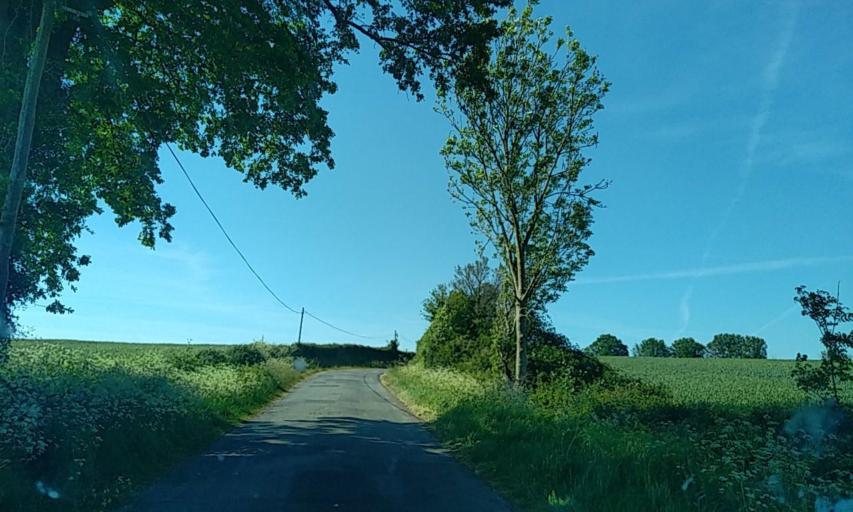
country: FR
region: Poitou-Charentes
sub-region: Departement des Deux-Sevres
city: Boisme
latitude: 46.7750
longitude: -0.4141
